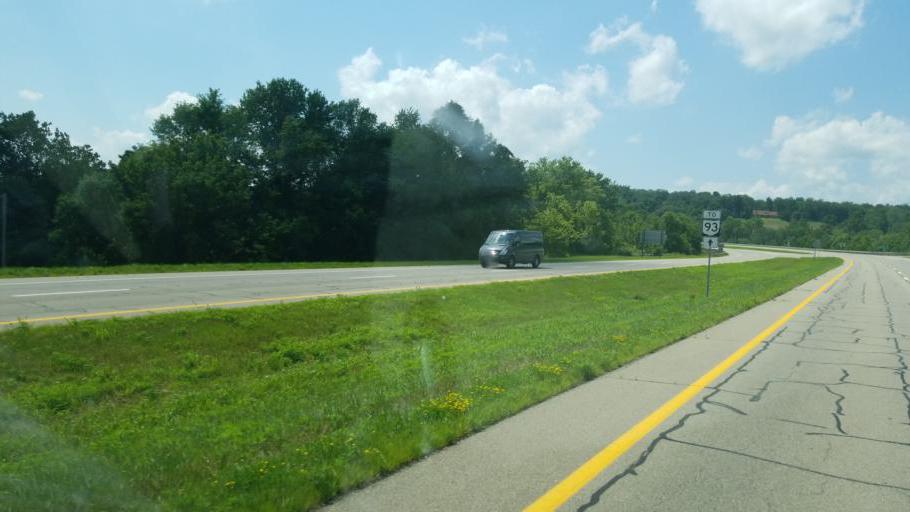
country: US
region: Ohio
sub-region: Coshocton County
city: West Lafayette
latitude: 40.2879
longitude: -81.7129
